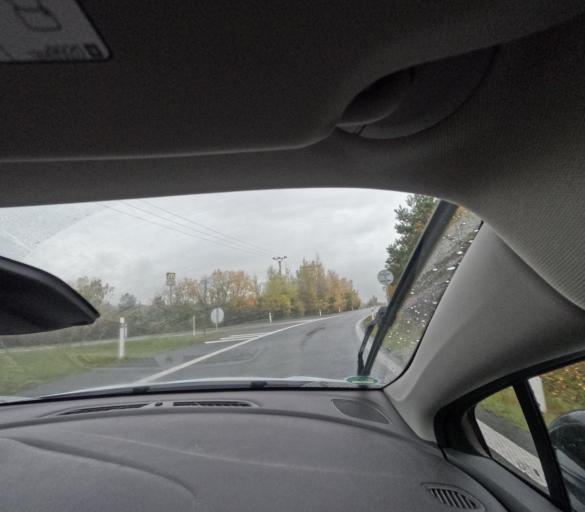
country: CZ
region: Central Bohemia
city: Velka Dobra
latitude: 50.1053
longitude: 14.0799
